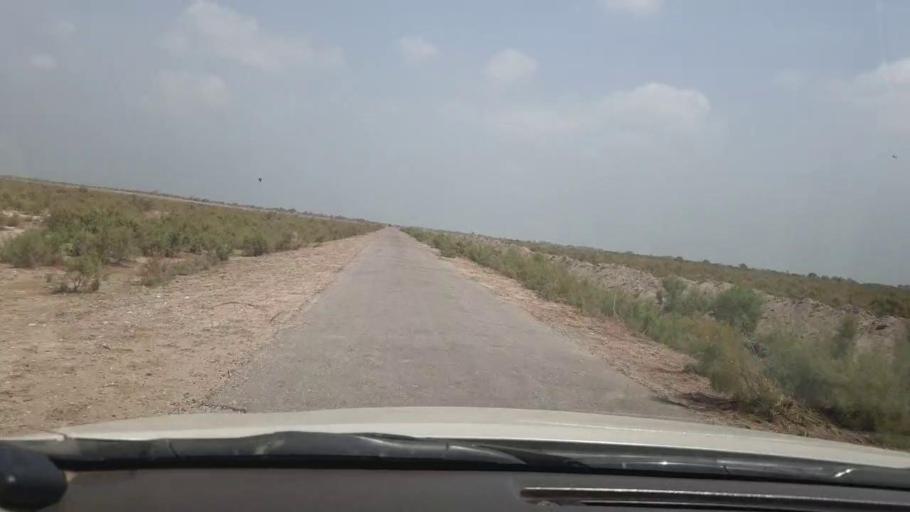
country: PK
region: Sindh
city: Garhi Yasin
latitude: 28.0216
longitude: 68.5004
